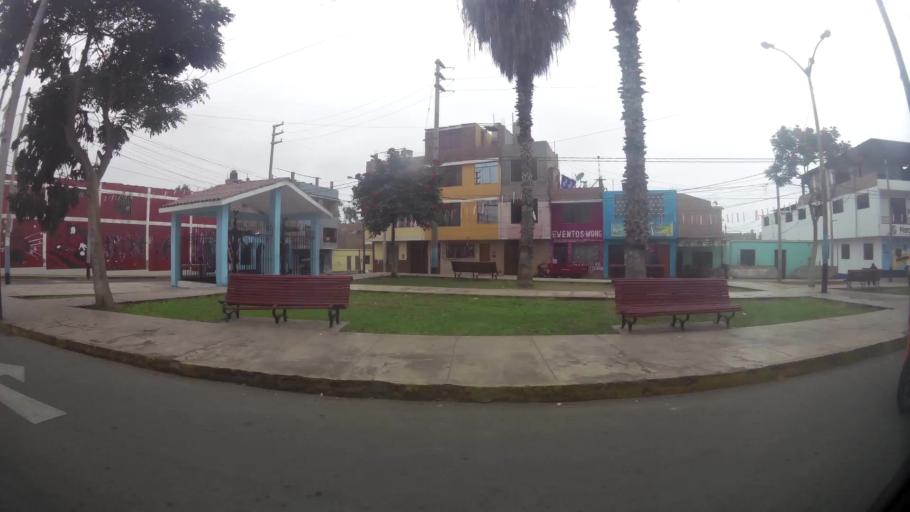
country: PE
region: Lima
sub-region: Provincia de Huaral
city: Chancay
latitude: -11.5645
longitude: -77.2661
